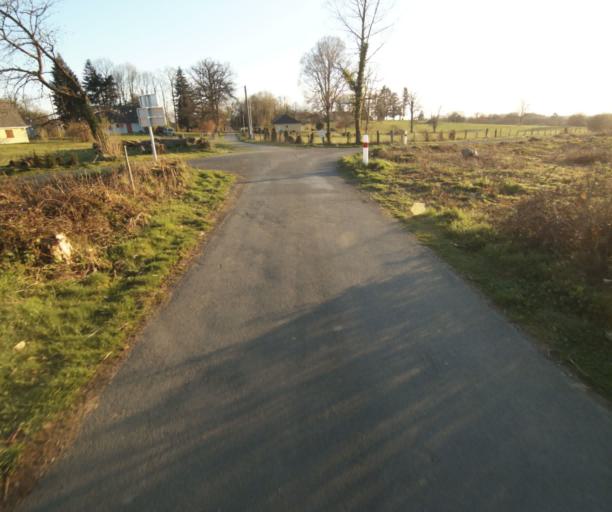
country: FR
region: Limousin
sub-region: Departement de la Correze
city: Uzerche
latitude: 45.3615
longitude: 1.5971
